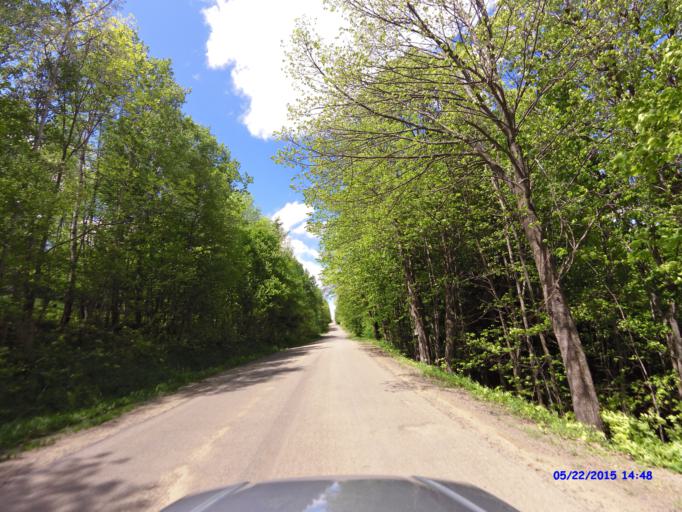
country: US
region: New York
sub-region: Cattaraugus County
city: Franklinville
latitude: 42.3501
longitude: -78.5844
